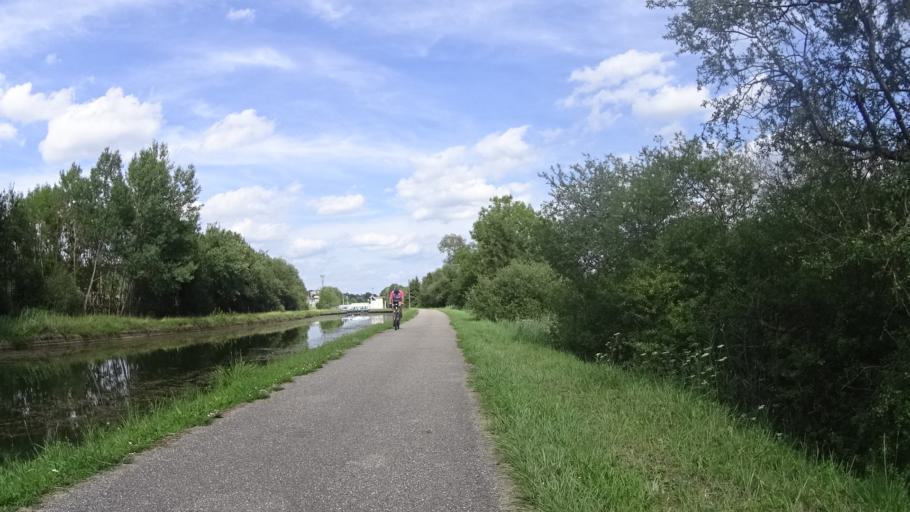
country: FR
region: Lorraine
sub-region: Departement de Meurthe-et-Moselle
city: Ecrouves
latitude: 48.6746
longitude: 5.8611
